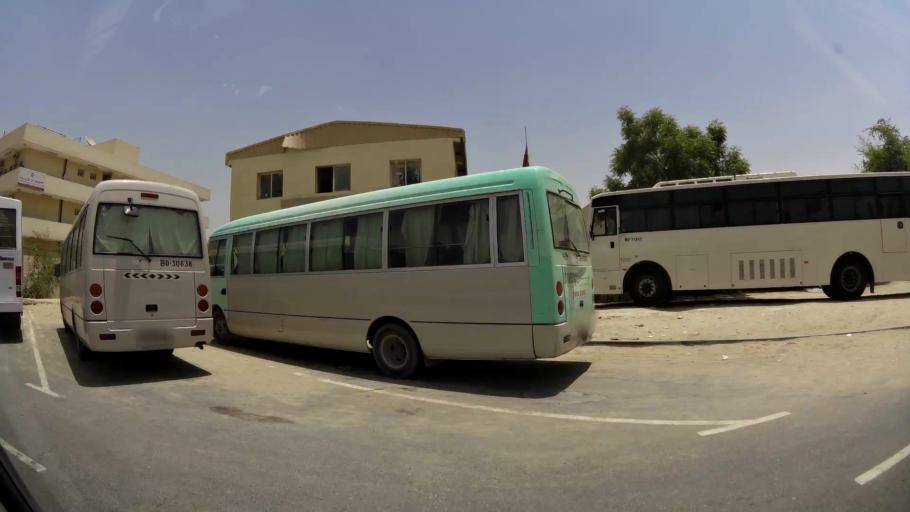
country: AE
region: Ash Shariqah
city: Sharjah
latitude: 25.2737
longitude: 55.4292
